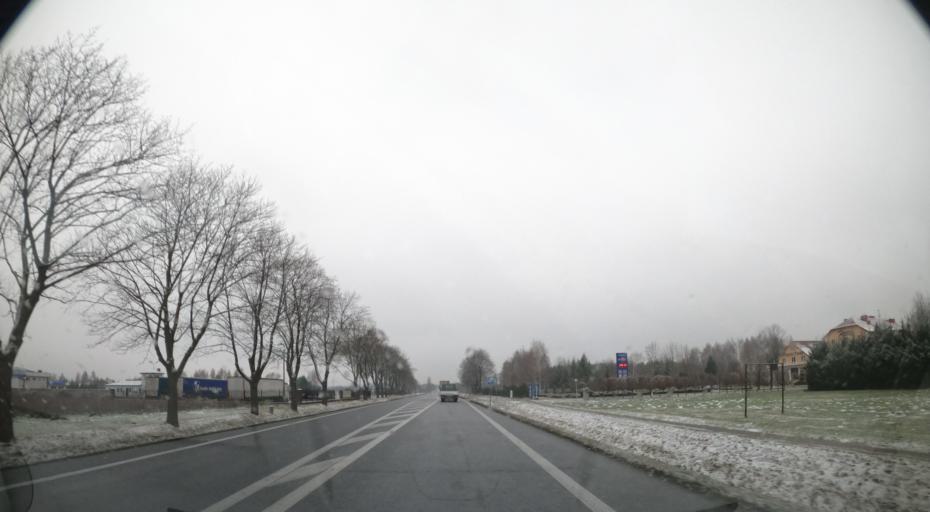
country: PL
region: Masovian Voivodeship
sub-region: Powiat sochaczewski
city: Paprotnia
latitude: 52.2103
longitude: 20.4487
